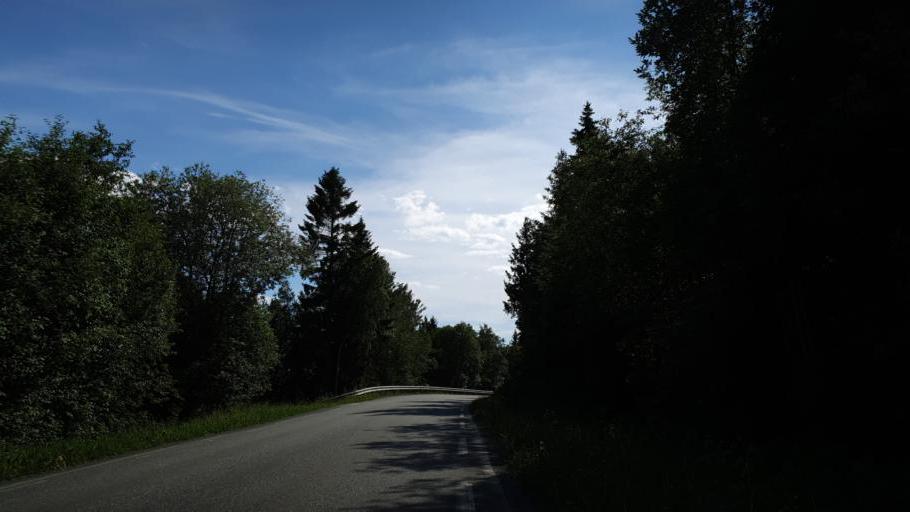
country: NO
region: Nord-Trondelag
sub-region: Leksvik
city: Leksvik
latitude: 63.6318
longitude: 10.5704
